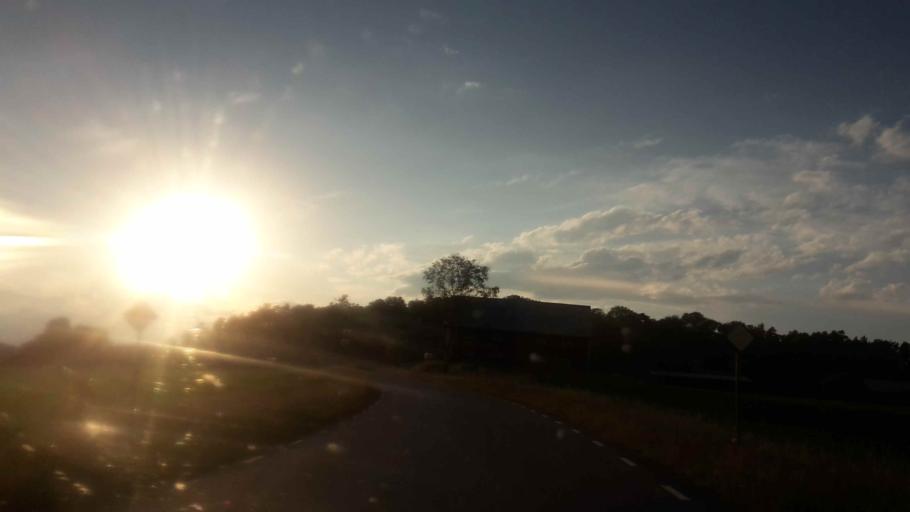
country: SE
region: OEstergoetland
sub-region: Valdemarsviks Kommun
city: Valdemarsvik
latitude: 58.3424
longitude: 16.6118
